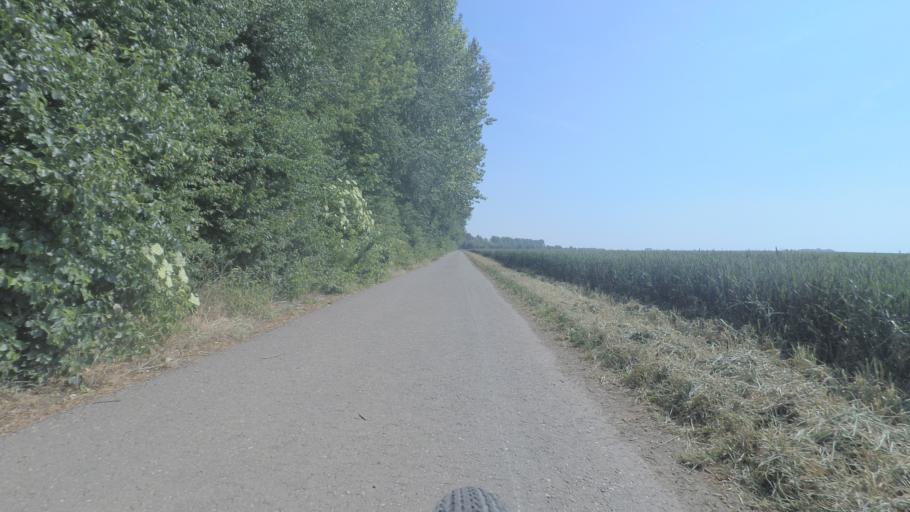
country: DE
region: Saxony-Anhalt
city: Gross Bornecke
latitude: 51.8516
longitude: 11.4690
